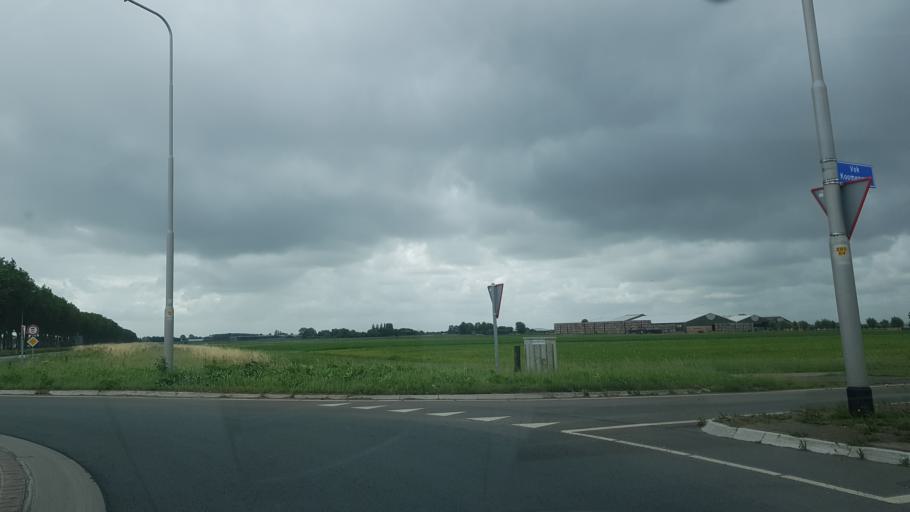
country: NL
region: North Holland
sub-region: Gemeente Medemblik
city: Medemblik
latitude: 52.7245
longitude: 5.1284
